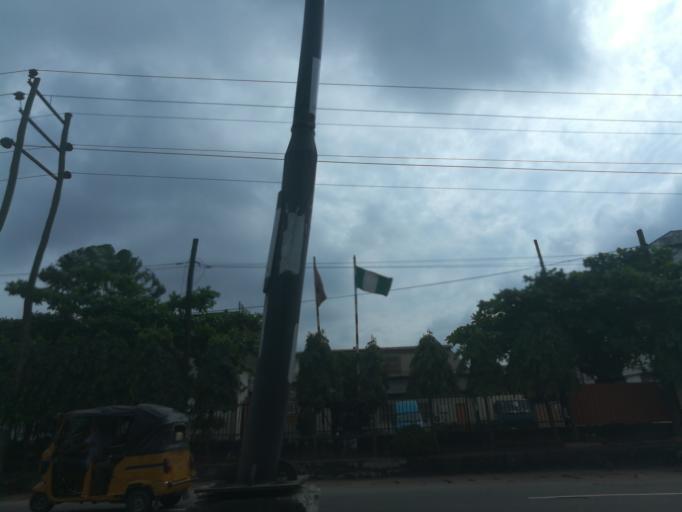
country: NG
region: Lagos
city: Ikeja
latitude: 6.6037
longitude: 3.3373
